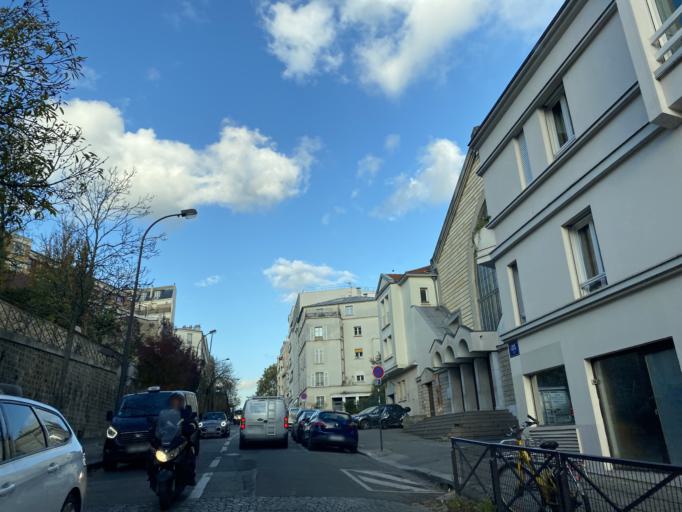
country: FR
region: Ile-de-France
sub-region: Departement de Seine-Saint-Denis
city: Bagnolet
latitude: 48.8603
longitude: 2.4043
